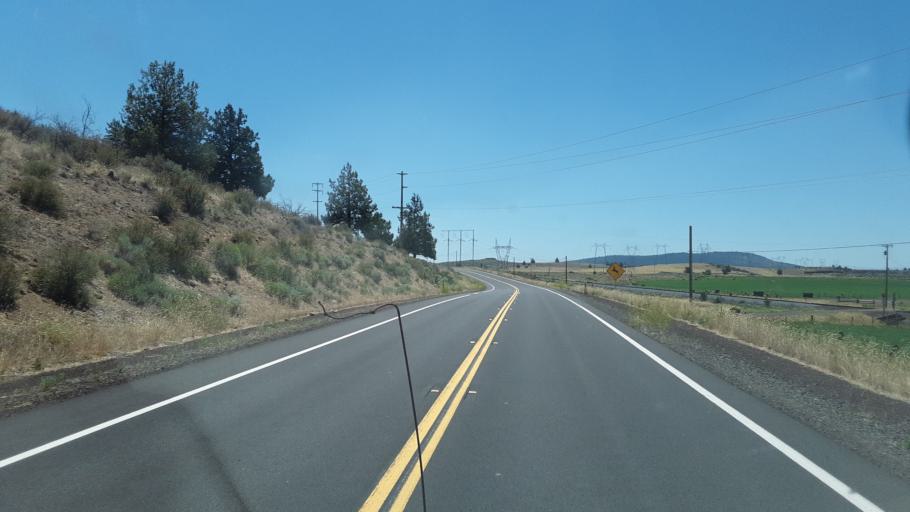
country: US
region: California
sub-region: Siskiyou County
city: Tulelake
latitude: 41.7230
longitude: -121.2944
